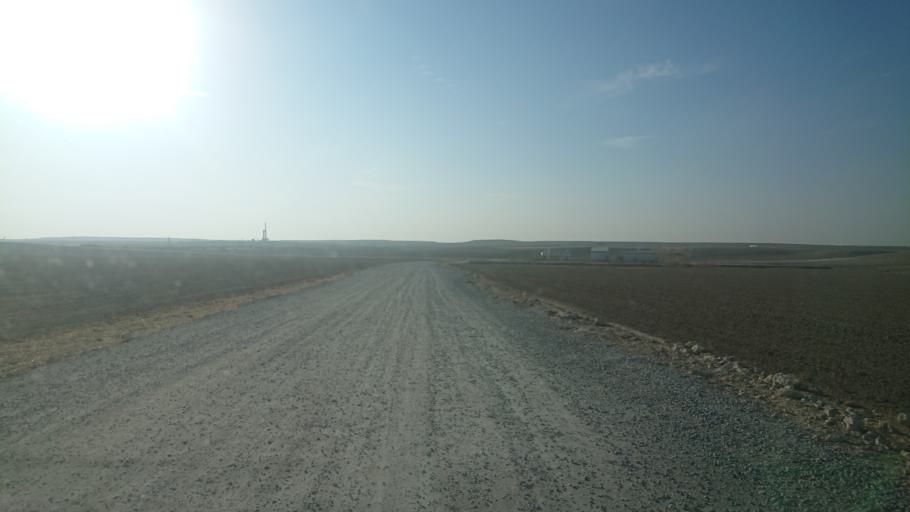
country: TR
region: Aksaray
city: Sultanhani
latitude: 38.0831
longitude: 33.6206
